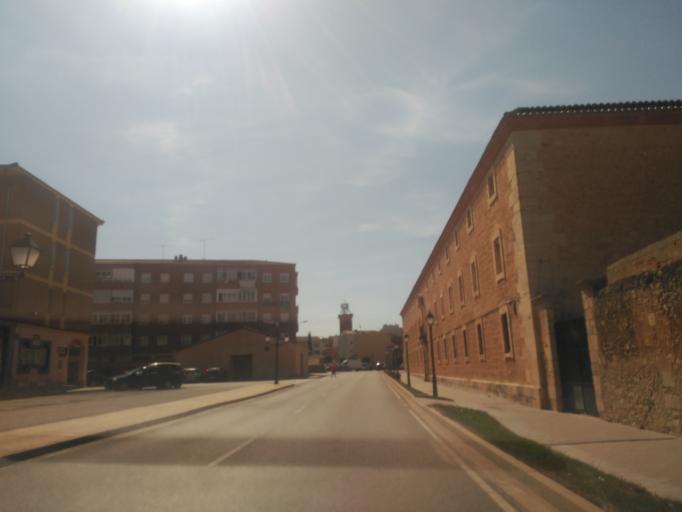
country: ES
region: Castille and Leon
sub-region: Provincia de Soria
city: El Burgo de Osma
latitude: 41.5907
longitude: -3.0630
